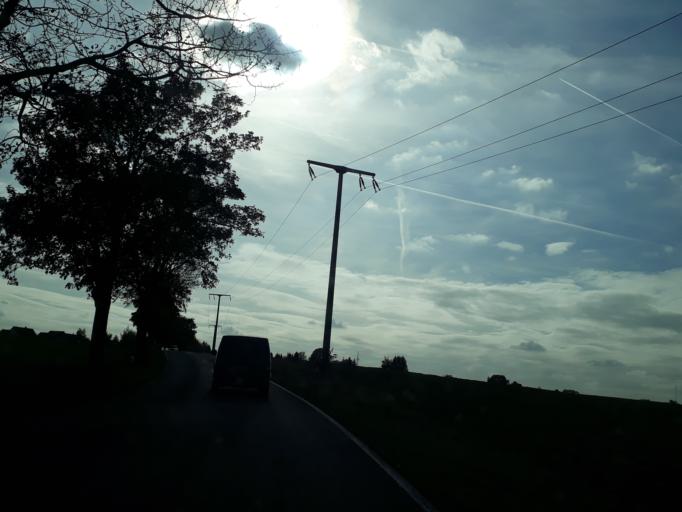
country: DE
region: Saxony
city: Klipphausen
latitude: 51.0724
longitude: 13.5765
